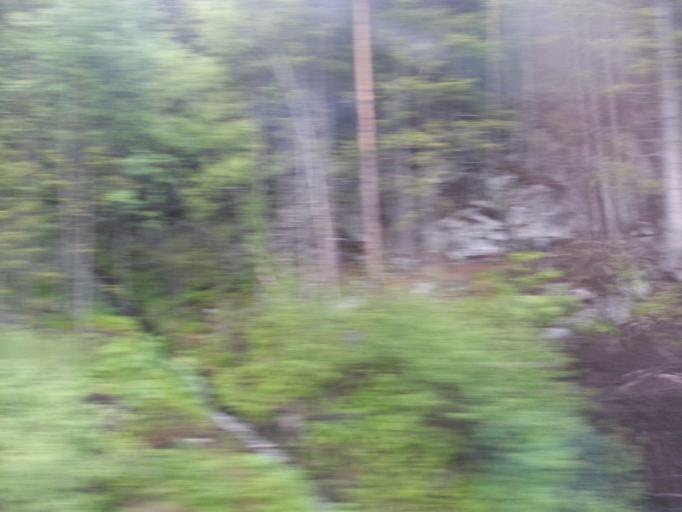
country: NO
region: Sor-Trondelag
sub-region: Rennebu
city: Berkak
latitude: 62.7717
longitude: 9.9898
